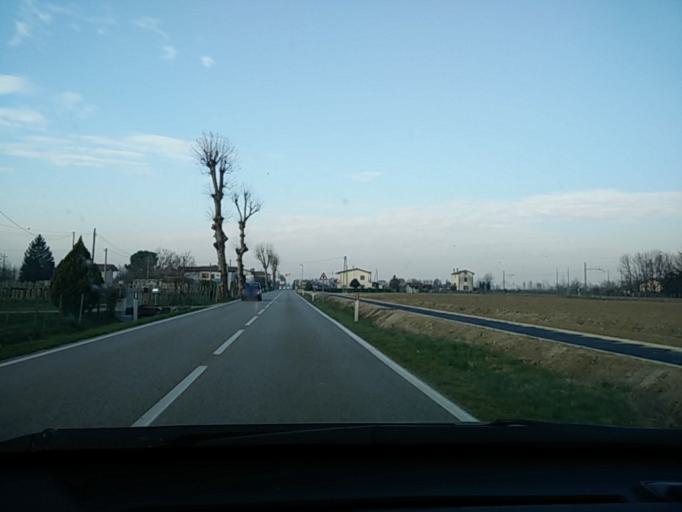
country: IT
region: Veneto
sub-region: Provincia di Treviso
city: Saletto-San Bartolomeo
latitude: 45.6972
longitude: 12.4179
